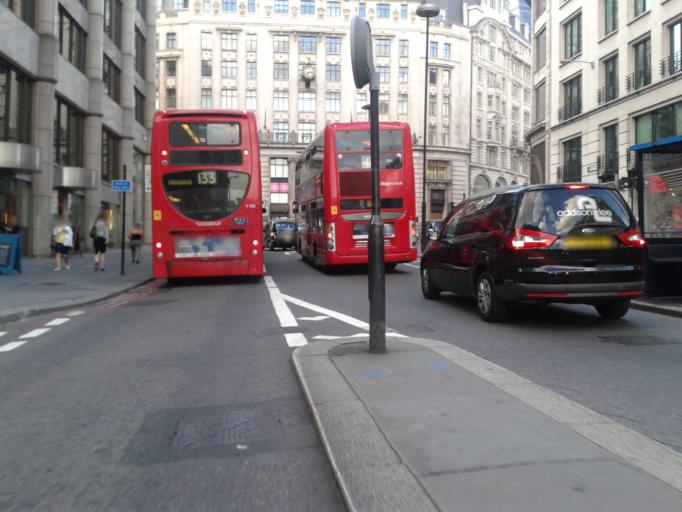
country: GB
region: England
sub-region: Greater London
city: City of London
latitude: 51.5103
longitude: -0.0869
